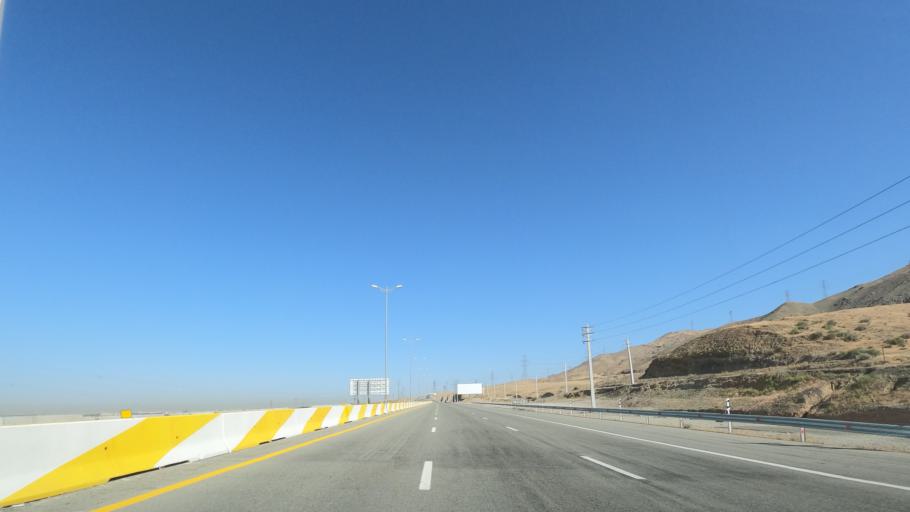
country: IR
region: Tehran
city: Shahr-e Qods
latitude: 35.7686
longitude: 51.0635
